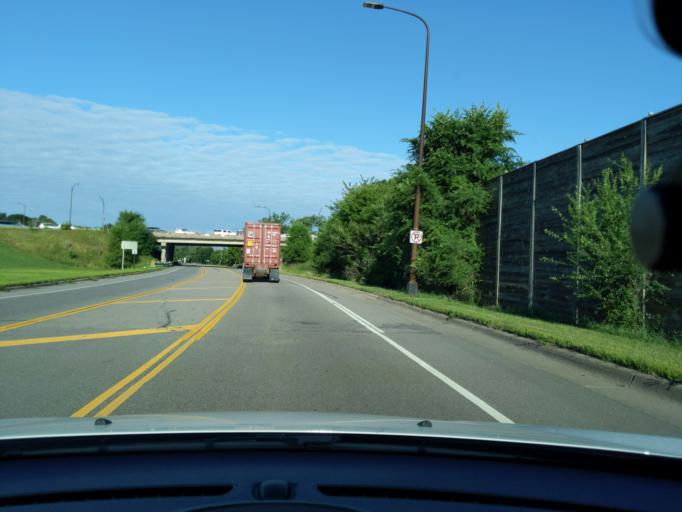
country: US
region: Minnesota
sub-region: Ramsey County
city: Falcon Heights
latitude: 44.9694
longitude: -93.1655
